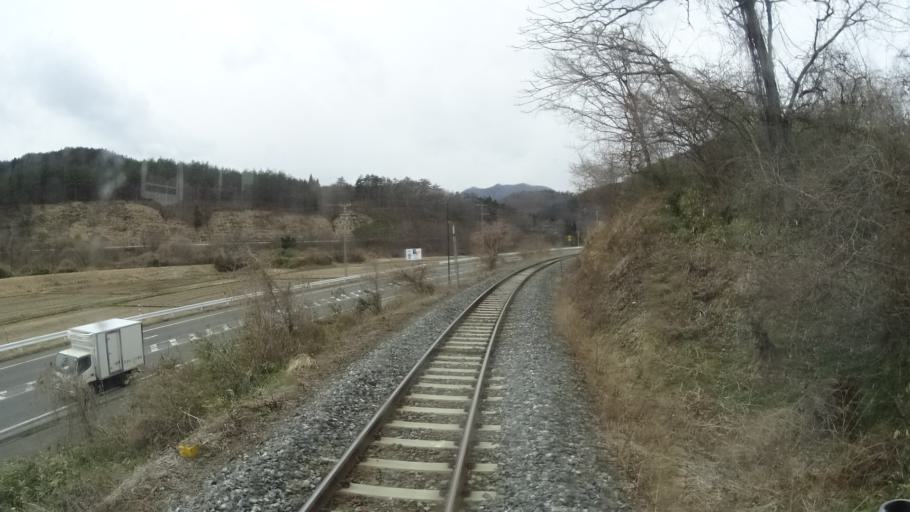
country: JP
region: Iwate
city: Tono
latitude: 39.3001
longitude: 141.3963
